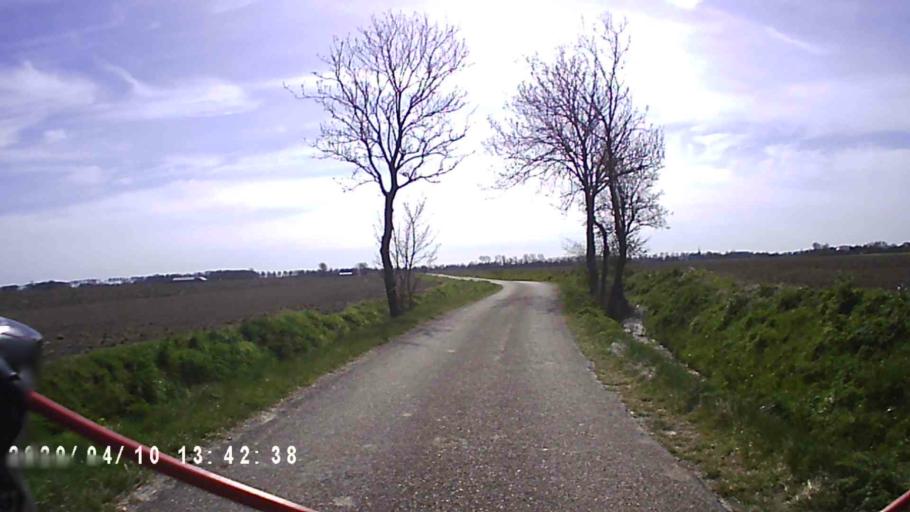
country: NL
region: Groningen
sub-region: Gemeente De Marne
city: Ulrum
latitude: 53.3736
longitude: 6.3830
